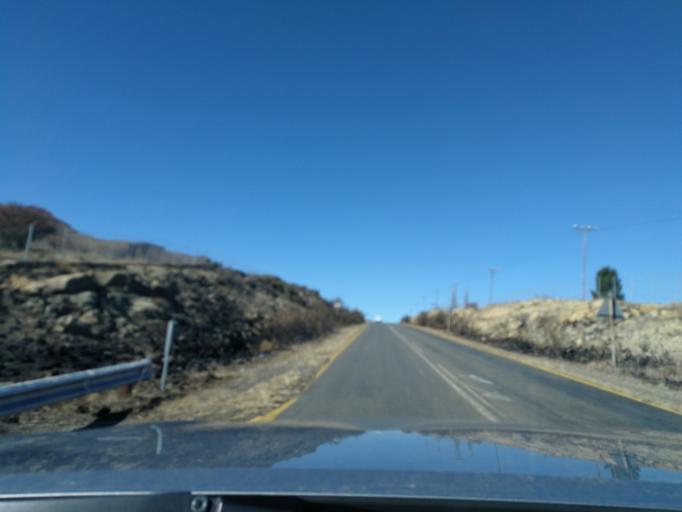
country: ZA
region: Orange Free State
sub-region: Thabo Mofutsanyana District Municipality
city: Bethlehem
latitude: -28.5142
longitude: 28.4324
